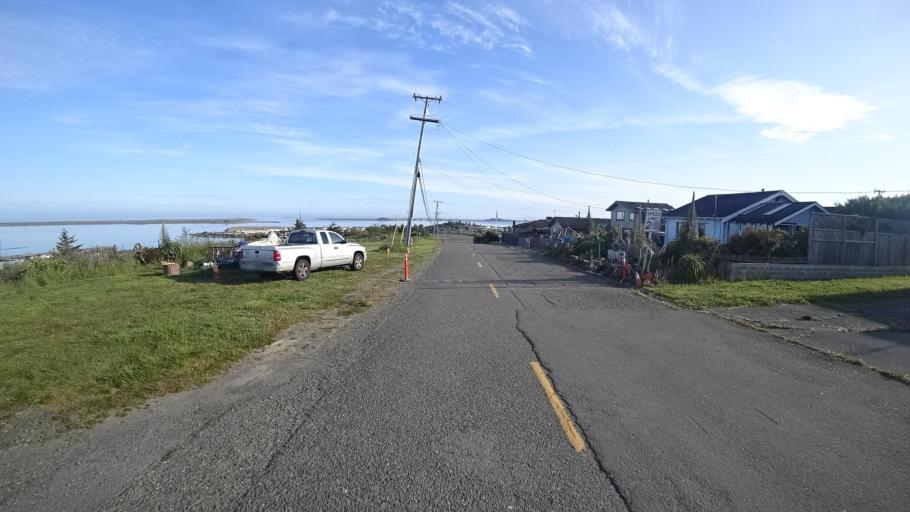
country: US
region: California
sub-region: Humboldt County
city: Humboldt Hill
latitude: 40.7297
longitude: -124.2132
